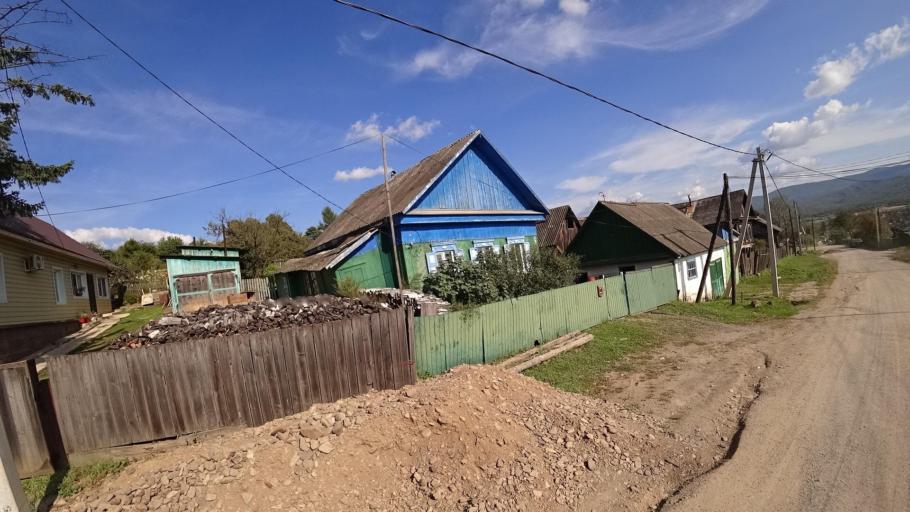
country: RU
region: Jewish Autonomous Oblast
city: Birakan
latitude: 48.9958
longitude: 131.7136
